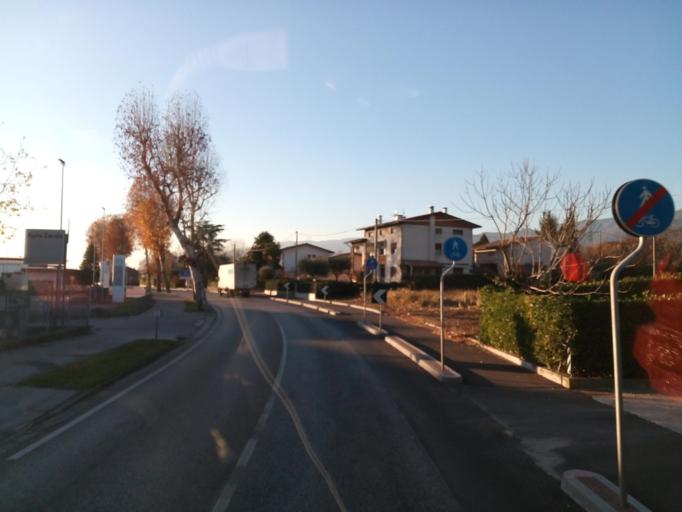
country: IT
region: Veneto
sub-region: Provincia di Treviso
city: San Zenone degli Ezzelini
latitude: 45.7793
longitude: 11.8272
